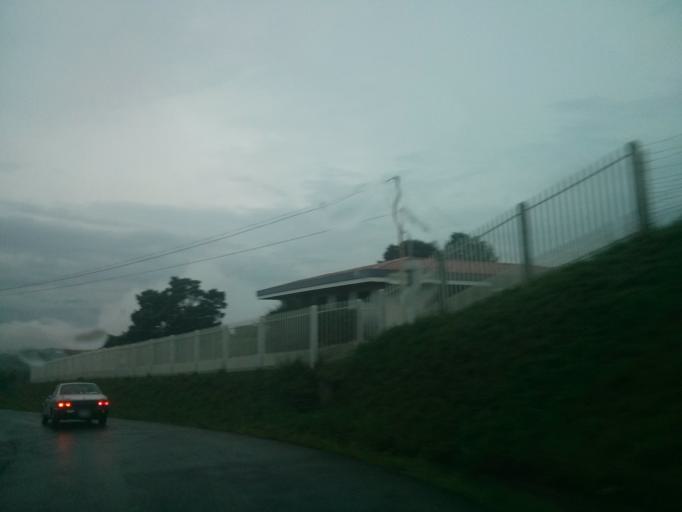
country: CR
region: Alajuela
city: Sabanilla
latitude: 10.0519
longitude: -84.2060
